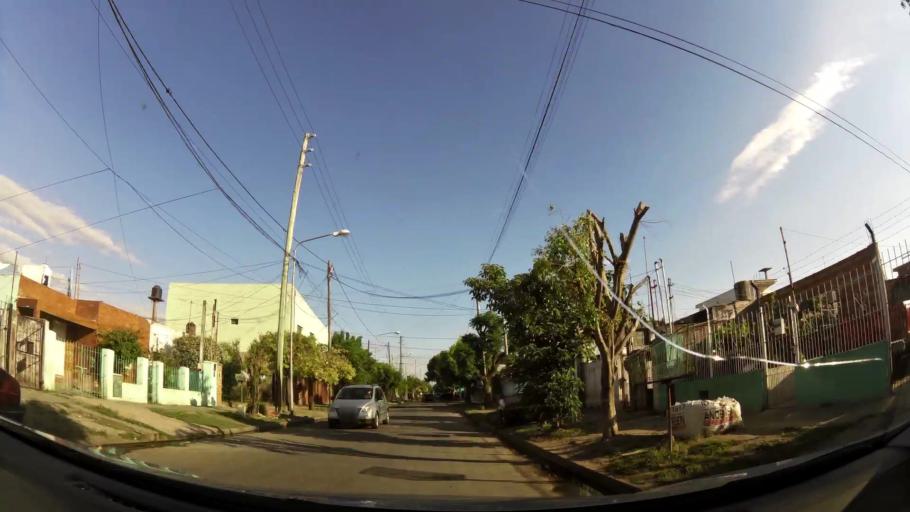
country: AR
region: Buenos Aires
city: Santa Catalina - Dique Lujan
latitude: -34.4646
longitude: -58.6642
